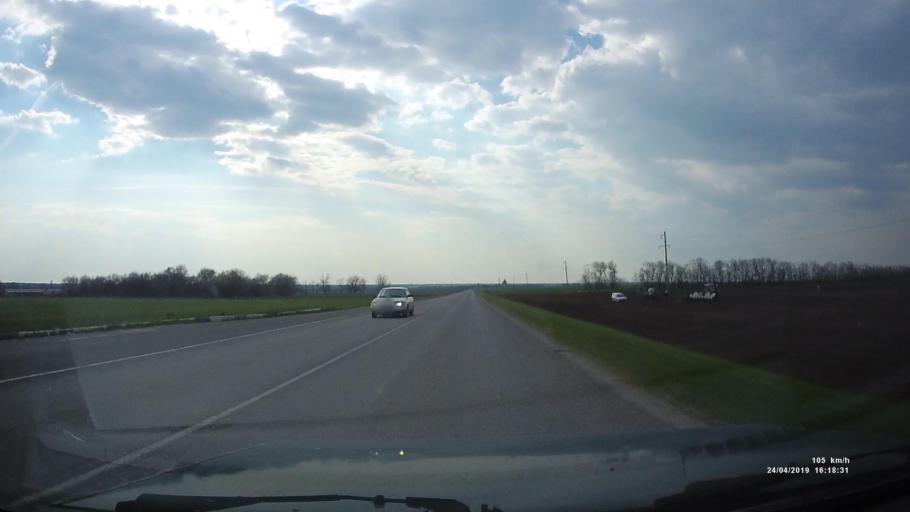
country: RU
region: Rostov
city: Sovetskoye
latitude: 46.7750
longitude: 42.1142
